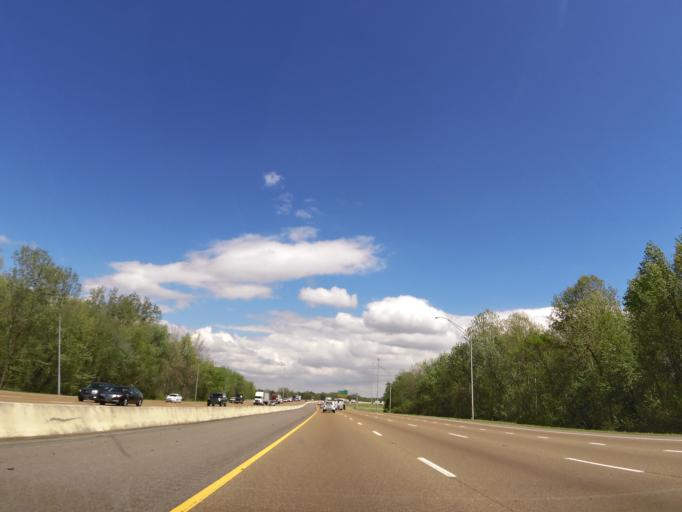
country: US
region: Tennessee
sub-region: Shelby County
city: Bartlett
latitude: 35.1912
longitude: -89.9349
